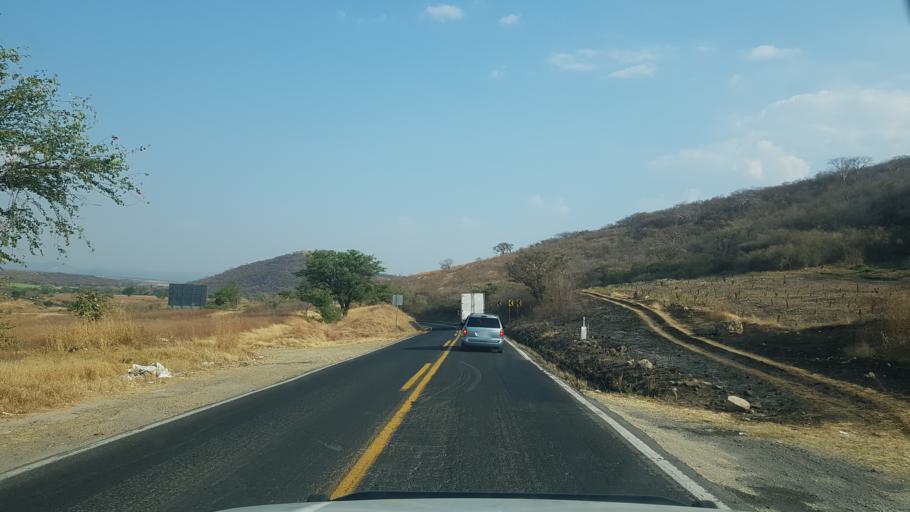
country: MX
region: Puebla
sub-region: Tilapa
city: San Felix Rijo
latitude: 18.6354
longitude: -98.5854
